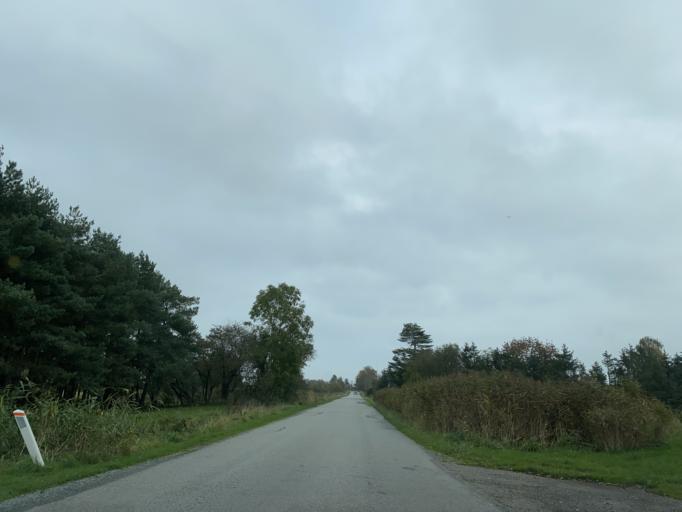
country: DK
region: South Denmark
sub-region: Aabenraa Kommune
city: Lojt Kirkeby
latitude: 55.1575
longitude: 9.4875
